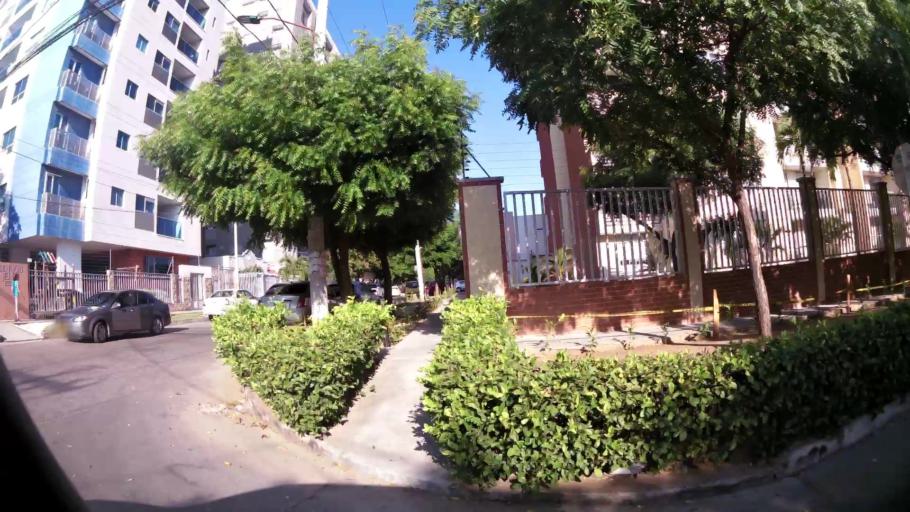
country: CO
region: Atlantico
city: Barranquilla
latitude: 11.0076
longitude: -74.7970
